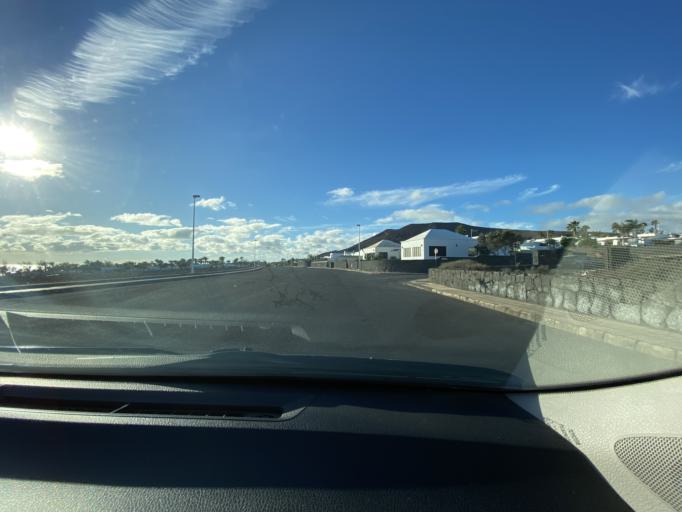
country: ES
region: Canary Islands
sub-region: Provincia de Las Palmas
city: Playa Blanca
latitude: 28.8637
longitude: -13.8443
